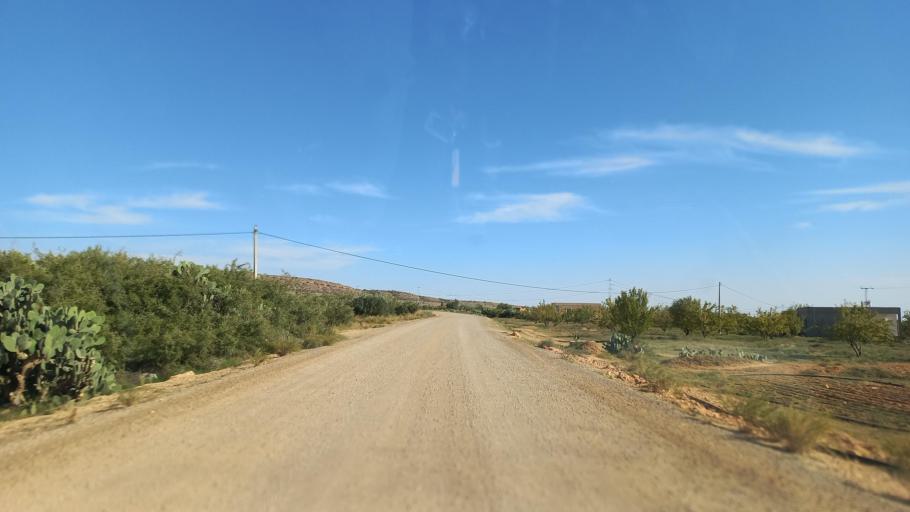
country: TN
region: Al Qasrayn
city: Sbiba
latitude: 35.2949
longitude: 9.1067
